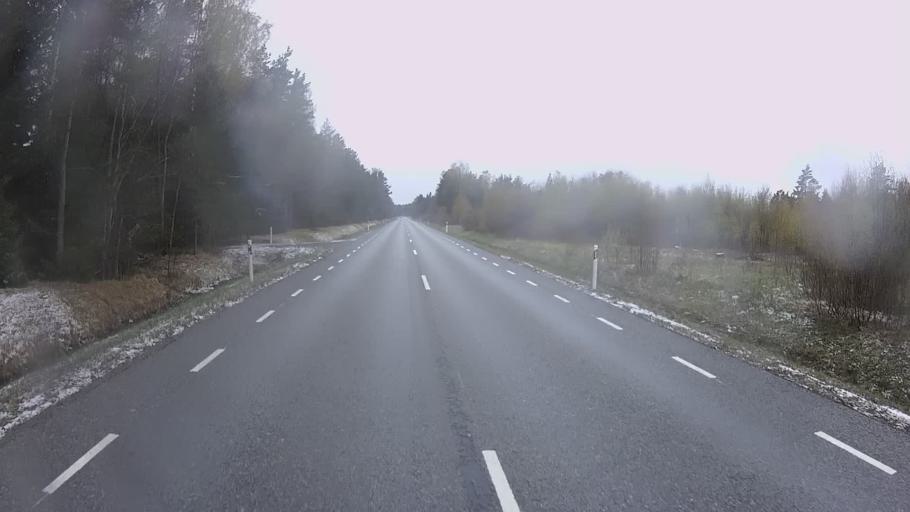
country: EE
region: Hiiumaa
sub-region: Kaerdla linn
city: Kardla
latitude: 59.0043
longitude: 22.5980
